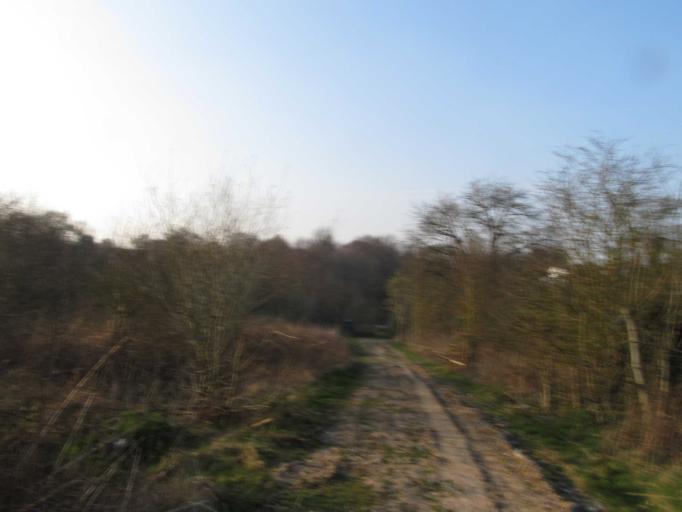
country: GB
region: Wales
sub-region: County of Flintshire
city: Buckley
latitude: 53.1984
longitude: -3.0888
